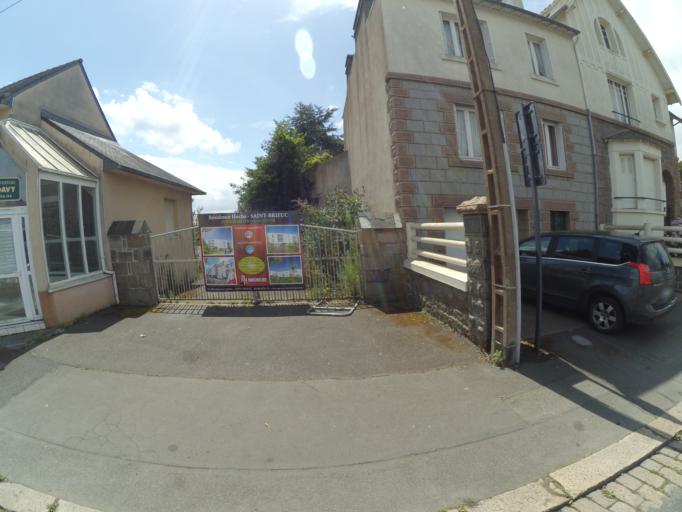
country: FR
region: Brittany
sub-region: Departement des Cotes-d'Armor
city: Saint-Brieuc
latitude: 48.5050
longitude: -2.7686
